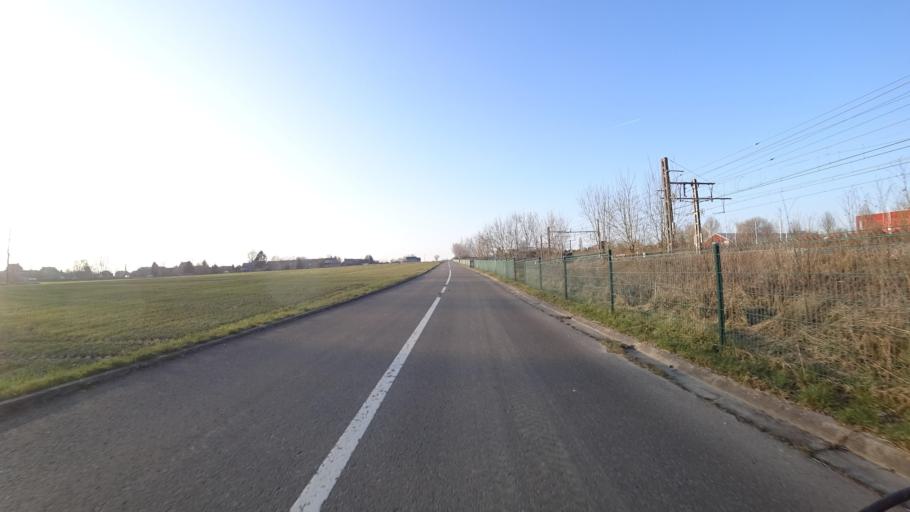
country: BE
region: Wallonia
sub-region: Province de Namur
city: Gembloux
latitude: 50.5752
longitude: 4.6860
